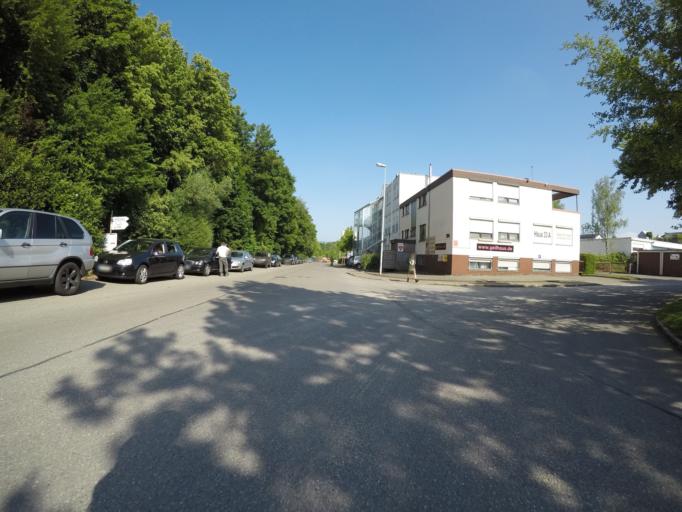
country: DE
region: Baden-Wuerttemberg
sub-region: Tuebingen Region
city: Wannweil
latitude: 48.4998
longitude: 9.1582
